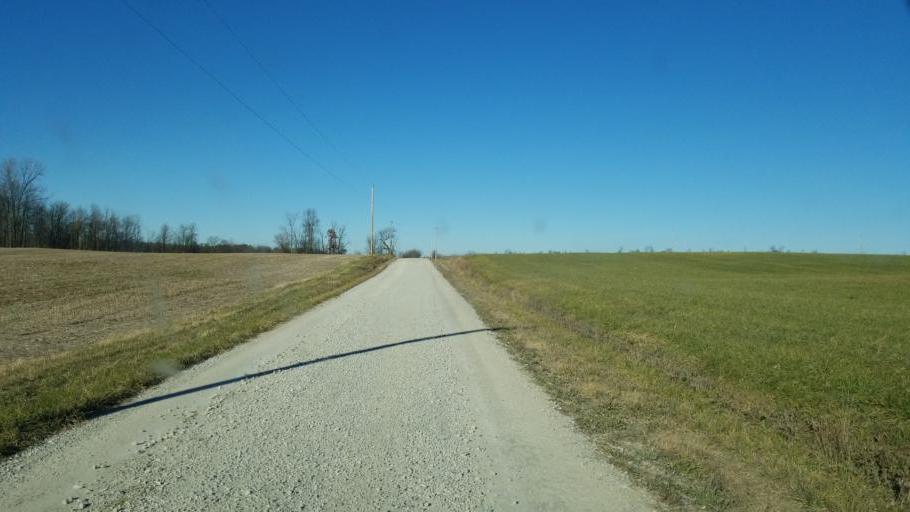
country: US
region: Ohio
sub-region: Morrow County
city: Mount Gilead
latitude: 40.5453
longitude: -82.7011
